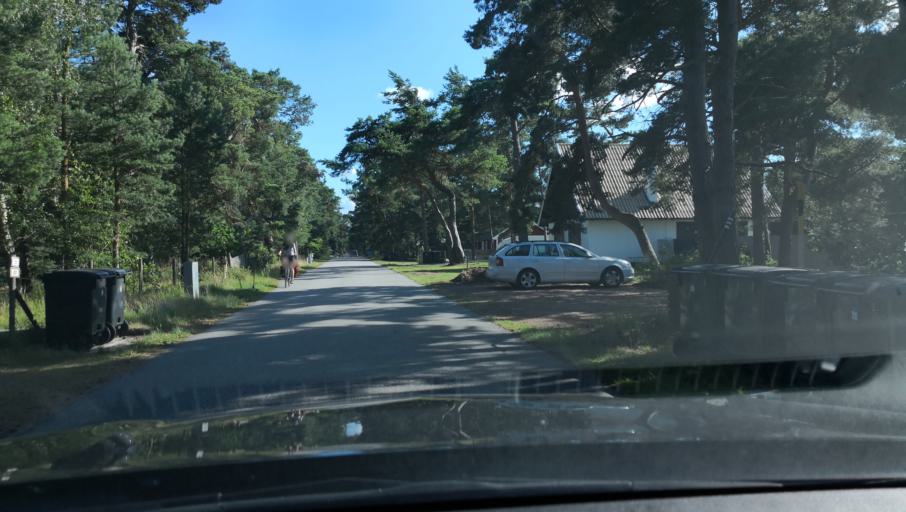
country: SE
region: Skane
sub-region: Simrishamns Kommun
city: Kivik
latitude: 55.7717
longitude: 14.1964
